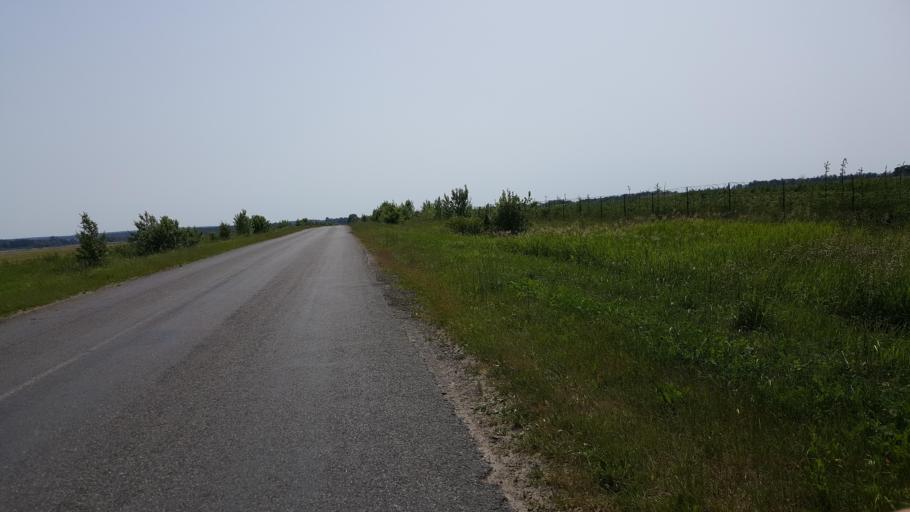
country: BY
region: Brest
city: Kamyanyets
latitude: 52.4198
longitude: 23.8060
